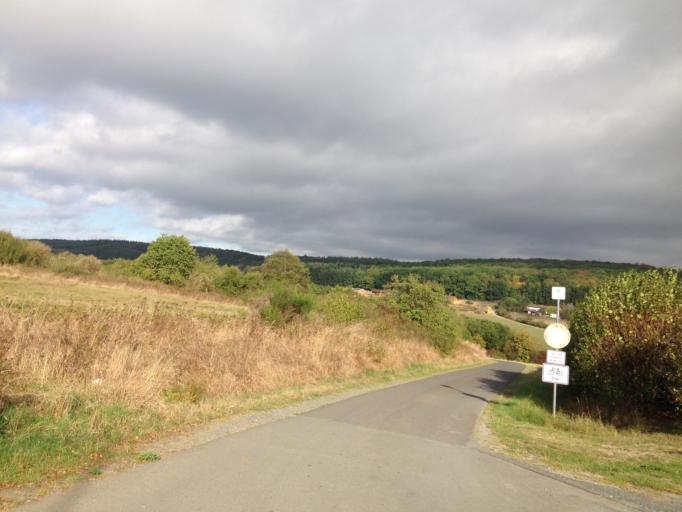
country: DE
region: Hesse
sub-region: Regierungsbezirk Giessen
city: Bad Endbach
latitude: 50.6791
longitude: 8.5210
